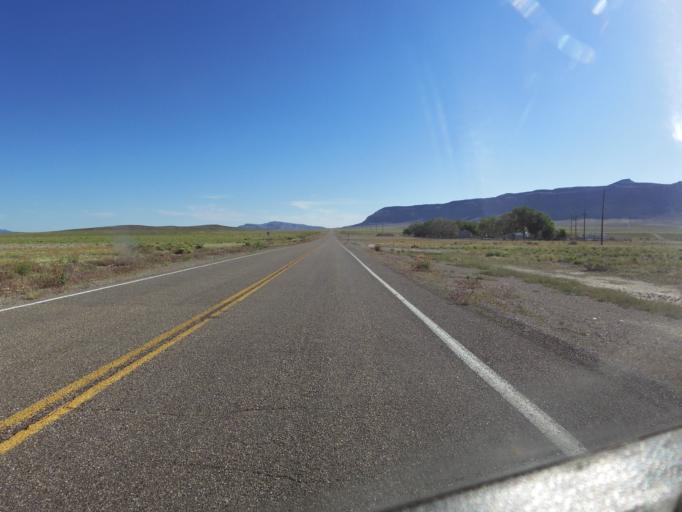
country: US
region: Nevada
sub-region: Nye County
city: Tonopah
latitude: 38.3701
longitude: -116.2283
